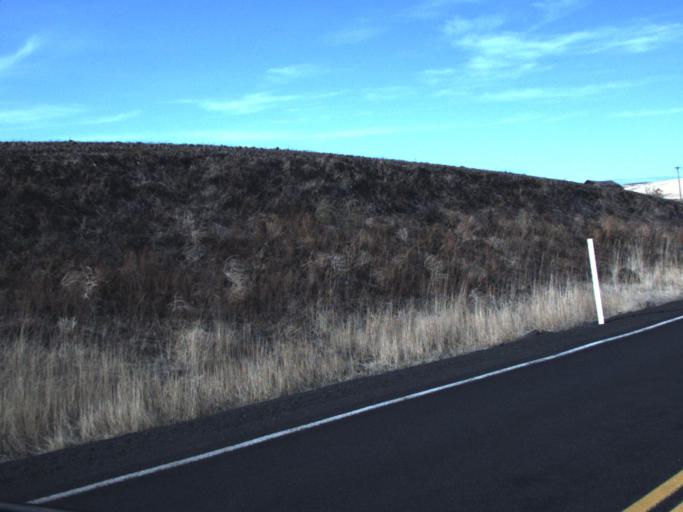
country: US
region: Washington
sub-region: Lincoln County
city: Davenport
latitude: 47.7019
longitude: -118.1410
